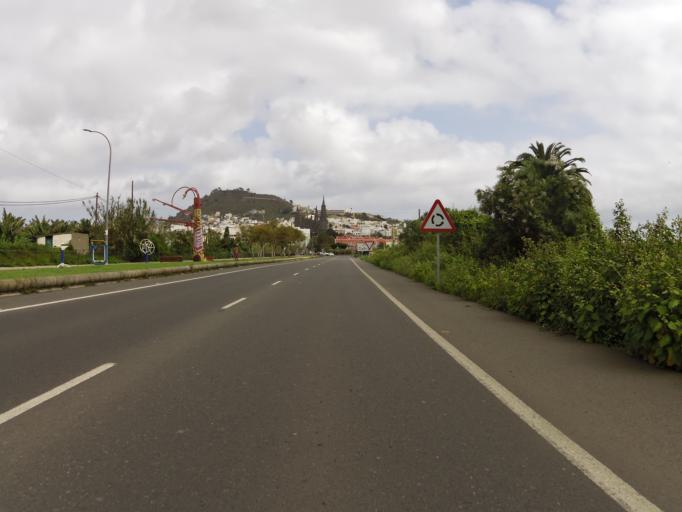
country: ES
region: Canary Islands
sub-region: Provincia de Las Palmas
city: Arucas
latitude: 28.1129
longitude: -15.5253
